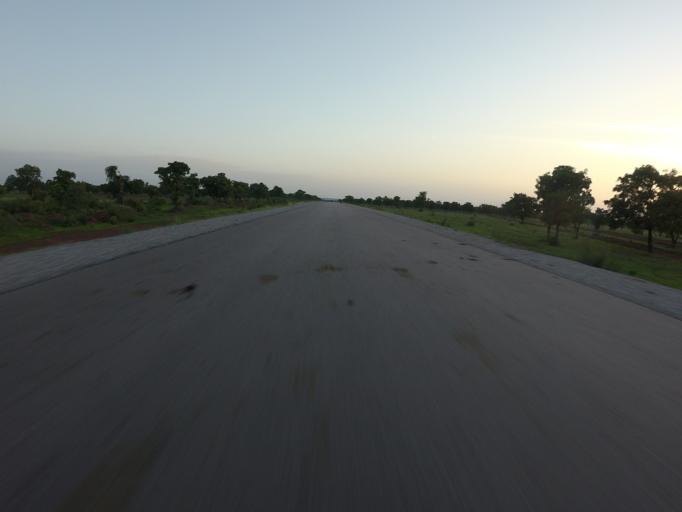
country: GH
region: Northern
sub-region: Yendi
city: Yendi
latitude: 9.9465
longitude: -0.1602
